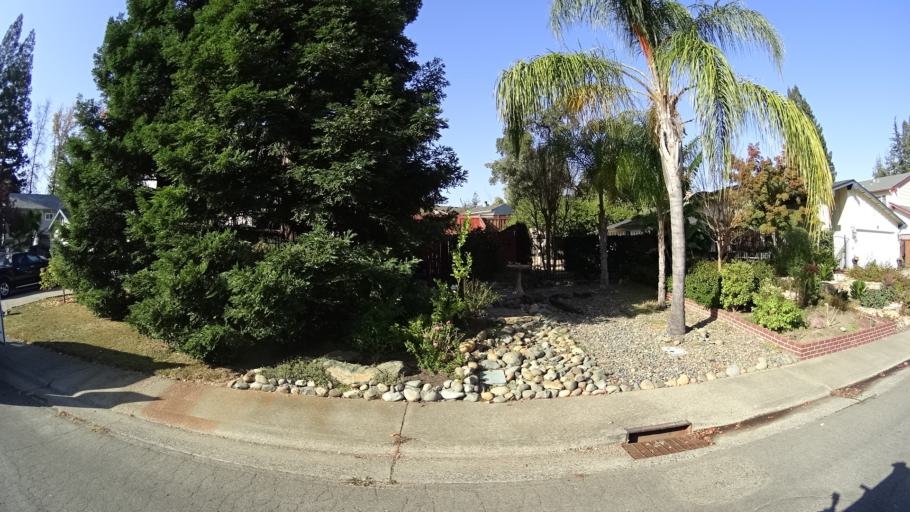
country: US
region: California
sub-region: Sacramento County
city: Orangevale
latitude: 38.6945
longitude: -121.2464
